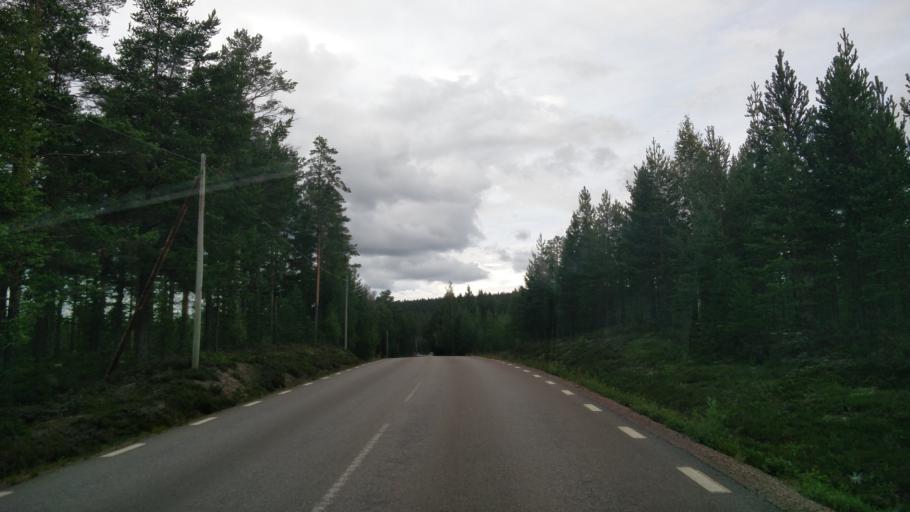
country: NO
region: Hedmark
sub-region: Trysil
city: Innbygda
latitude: 61.1732
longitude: 12.8467
